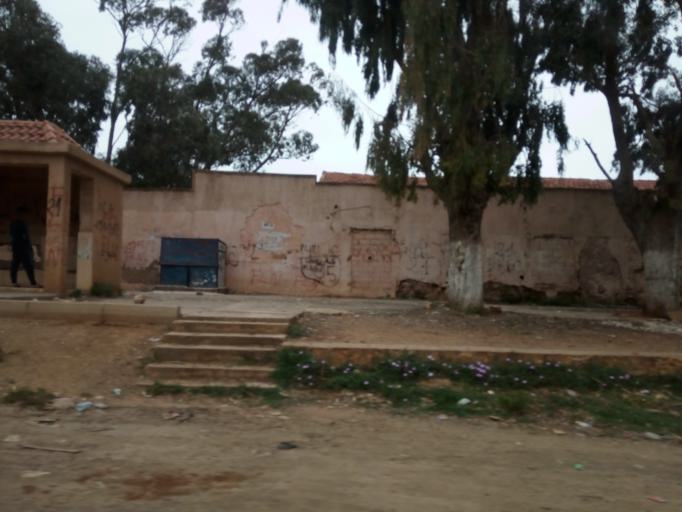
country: DZ
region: Tipaza
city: Tipasa
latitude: 36.5898
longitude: 2.5465
